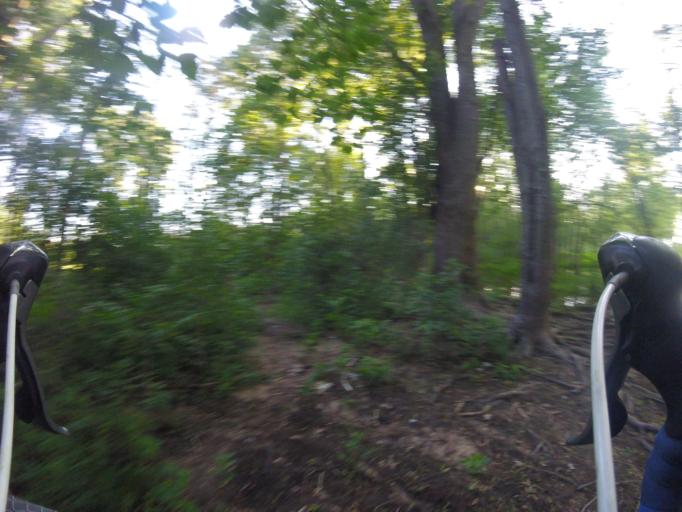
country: CA
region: Ontario
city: Bells Corners
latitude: 45.3609
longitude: -75.8715
